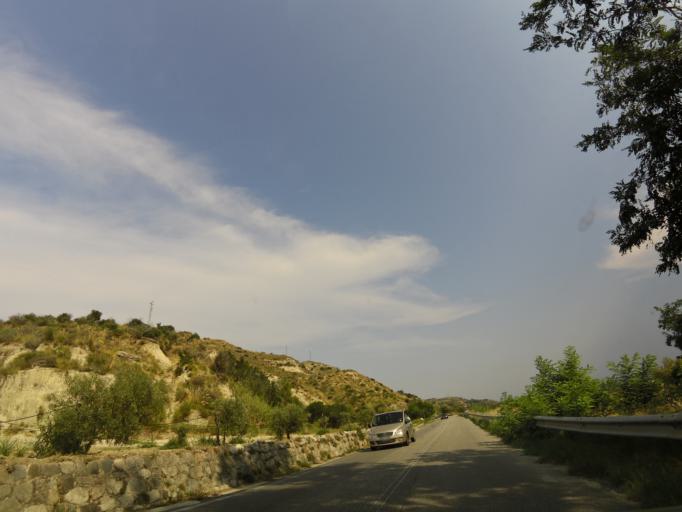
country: IT
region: Calabria
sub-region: Provincia di Reggio Calabria
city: Monasterace
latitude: 38.4645
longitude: 16.5133
